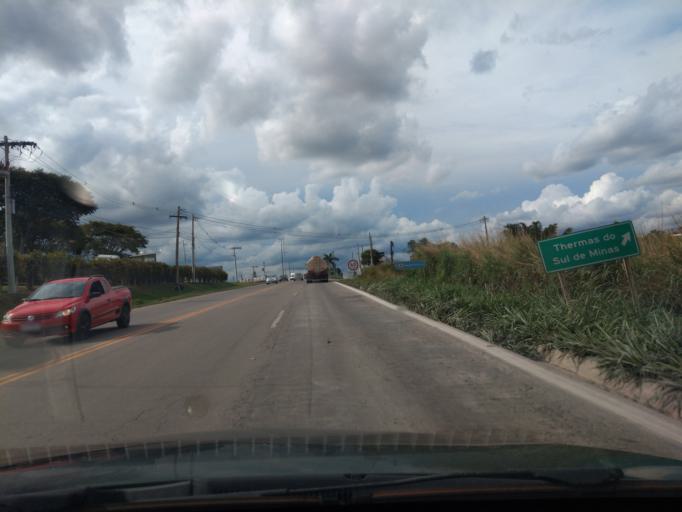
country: BR
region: Minas Gerais
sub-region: Varginha
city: Varginha
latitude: -21.5991
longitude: -45.4386
